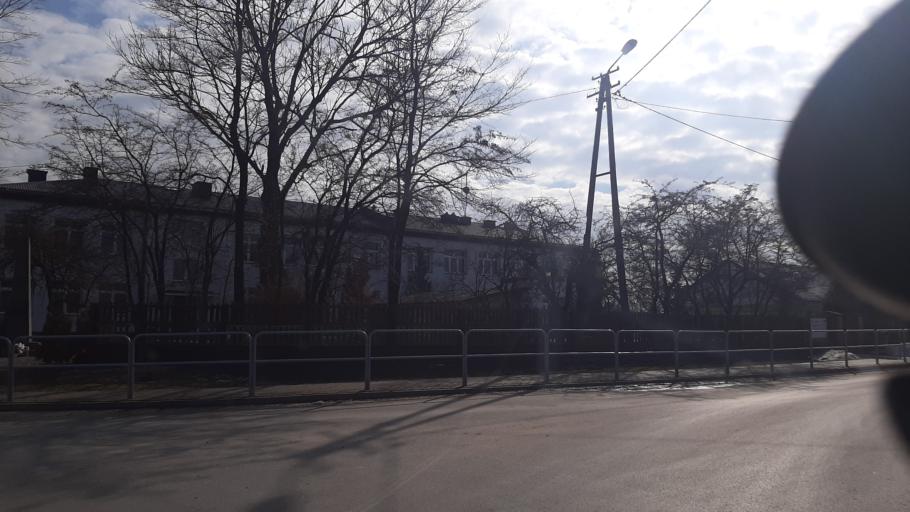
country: PL
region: Lublin Voivodeship
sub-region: Powiat lubartowski
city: Uscimow Stary
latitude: 51.4719
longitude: 22.9424
